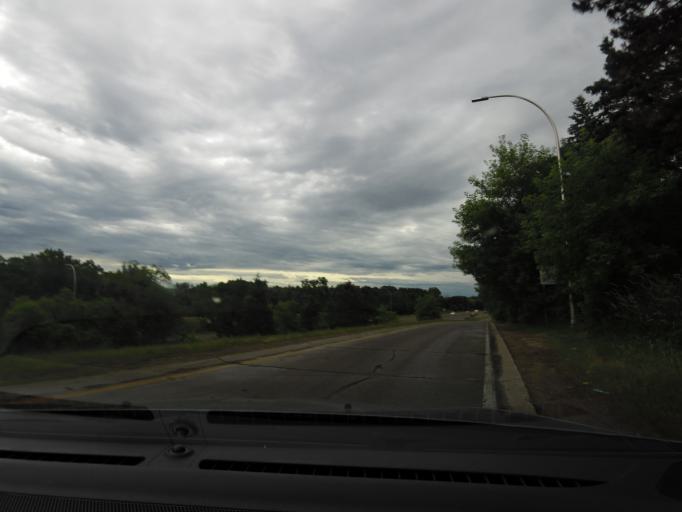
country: US
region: Minnesota
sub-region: Dakota County
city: South Saint Paul
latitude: 44.9123
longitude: -93.0652
